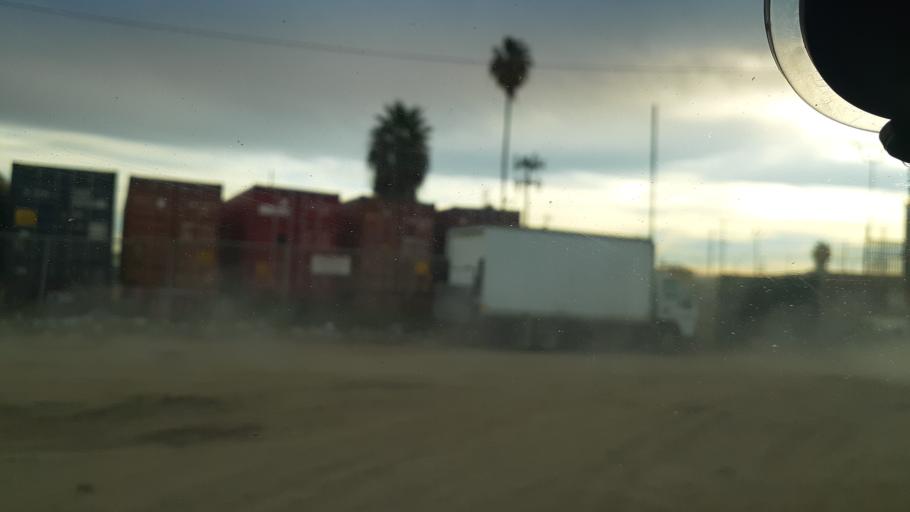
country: US
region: California
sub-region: Los Angeles County
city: Long Beach
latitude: 33.7830
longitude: -118.2306
